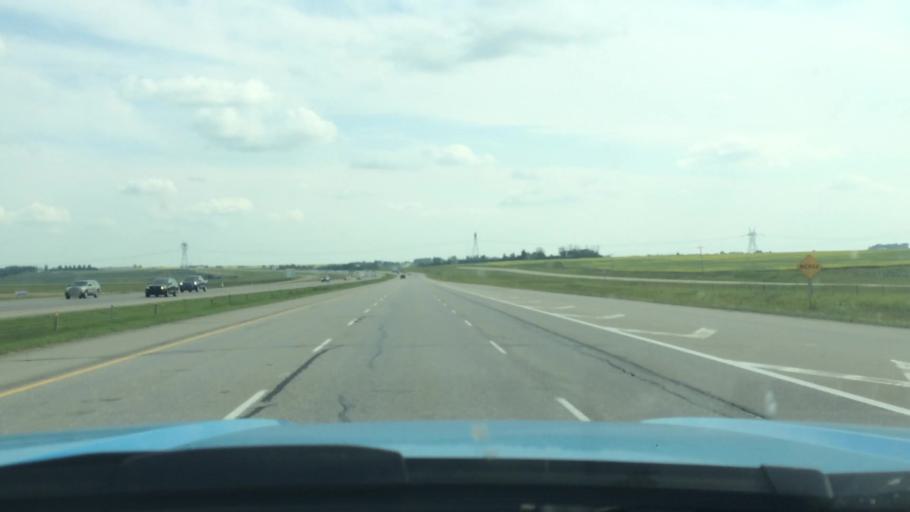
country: CA
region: Alberta
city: Crossfield
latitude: 51.4678
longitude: -114.0264
